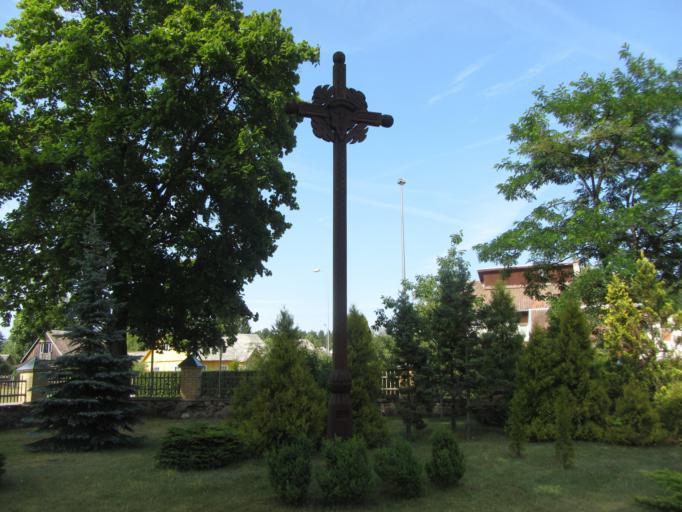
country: LT
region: Alytaus apskritis
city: Druskininkai
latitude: 54.0000
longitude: 24.0180
